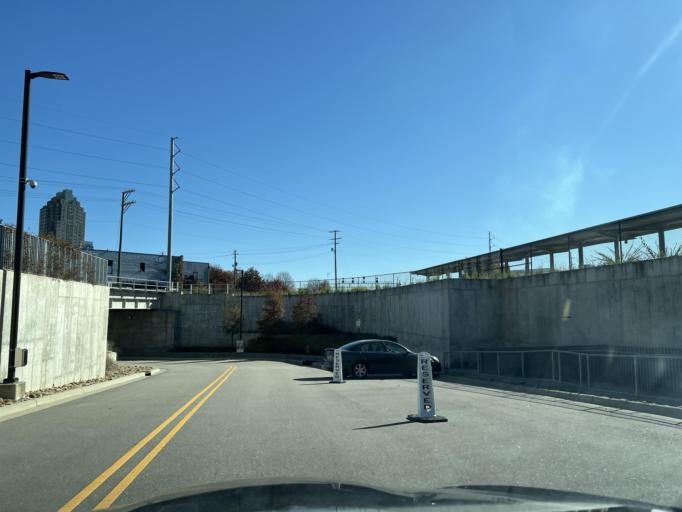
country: US
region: North Carolina
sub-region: Wake County
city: Raleigh
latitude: 35.7766
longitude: -78.6470
